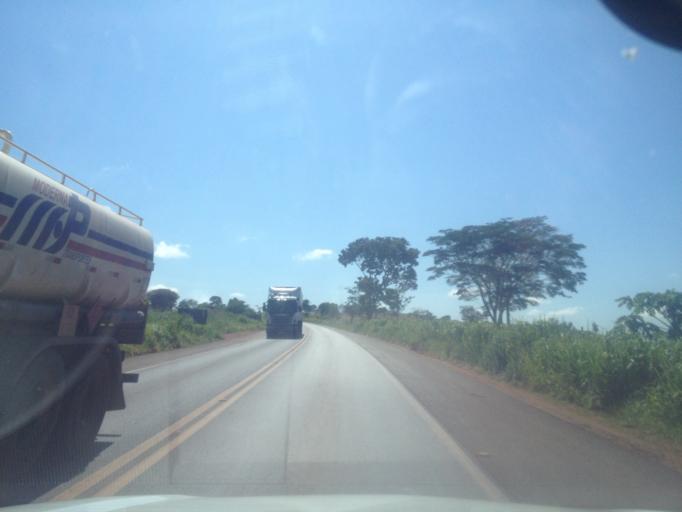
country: BR
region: Minas Gerais
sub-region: Santa Vitoria
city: Santa Vitoria
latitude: -19.0471
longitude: -50.4901
